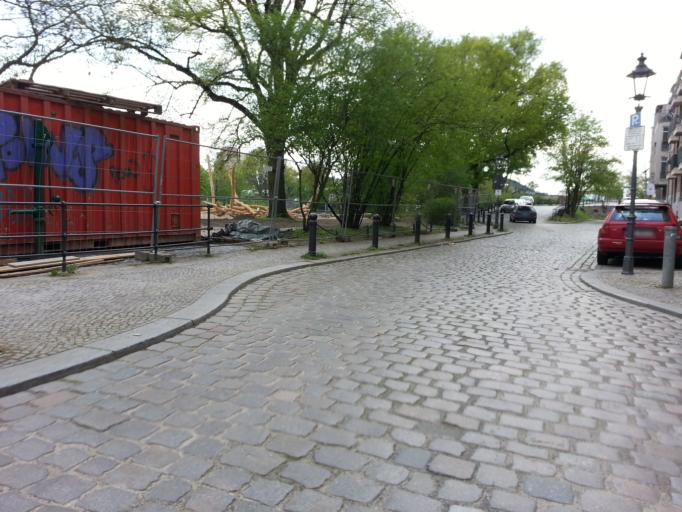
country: DE
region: Berlin
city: Spandau
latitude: 52.5365
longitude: 13.2069
